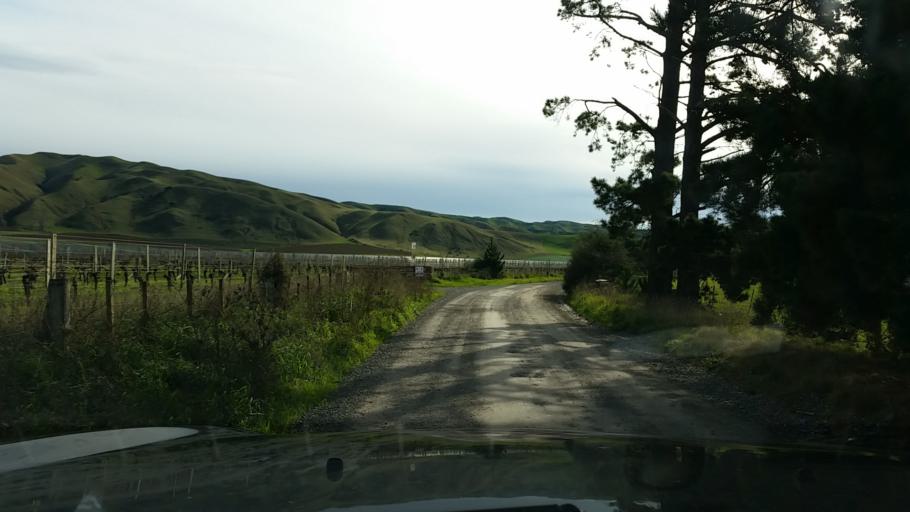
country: NZ
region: Marlborough
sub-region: Marlborough District
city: Blenheim
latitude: -41.6276
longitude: 174.1010
